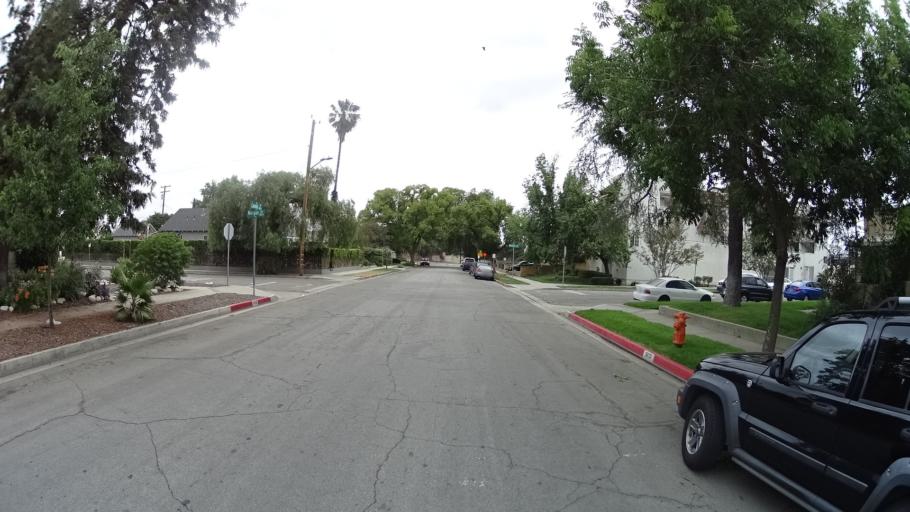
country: US
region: California
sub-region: Los Angeles County
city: Burbank
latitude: 34.1942
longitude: -118.3288
